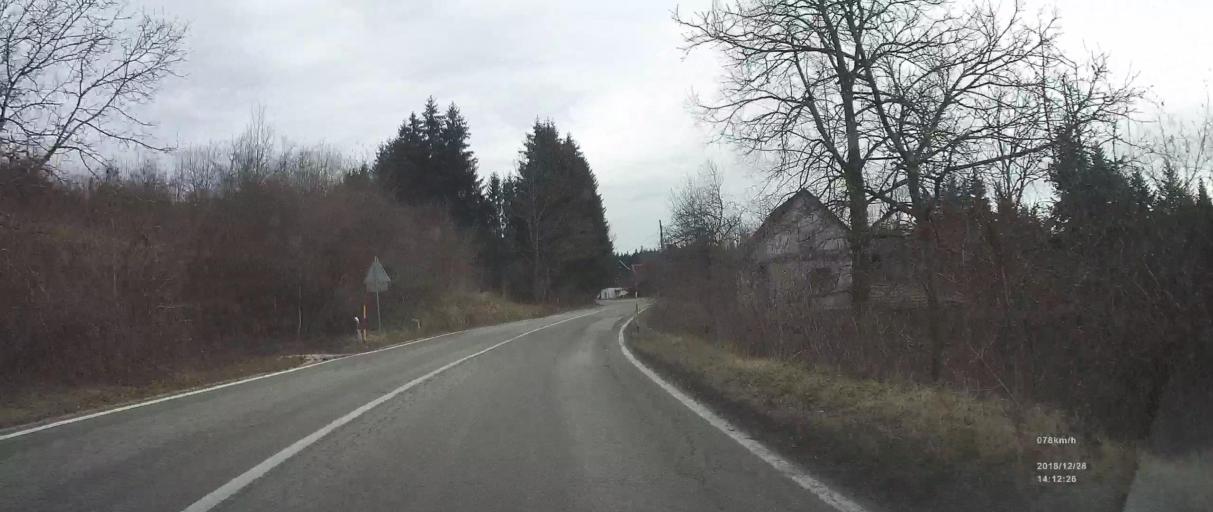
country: SI
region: Kostel
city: Kostel
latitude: 45.4452
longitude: 14.9991
